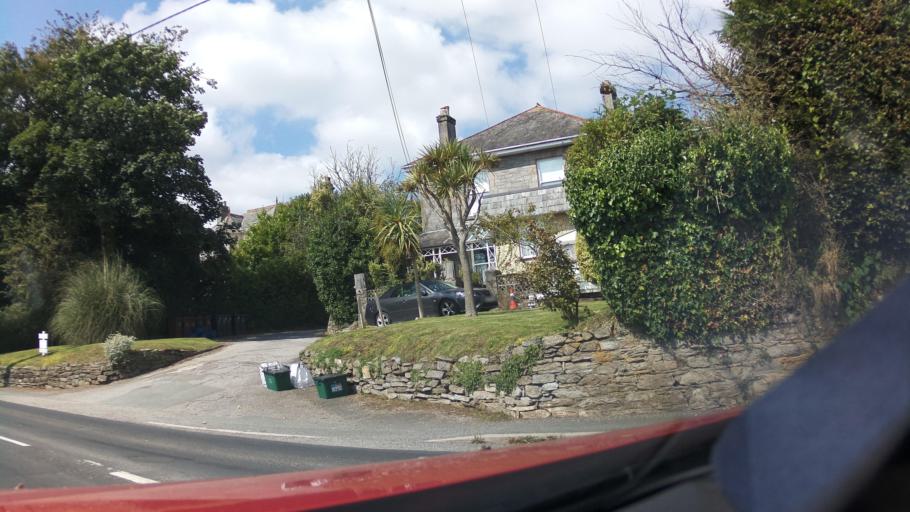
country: GB
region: England
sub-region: Devon
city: Yealmpton
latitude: 50.3507
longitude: -4.0387
